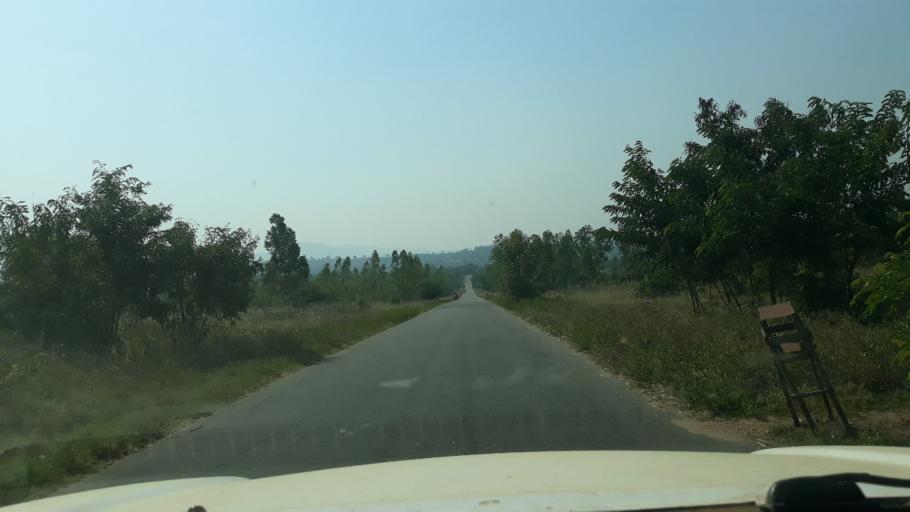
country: CD
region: South Kivu
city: Uvira
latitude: -3.1939
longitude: 29.1541
